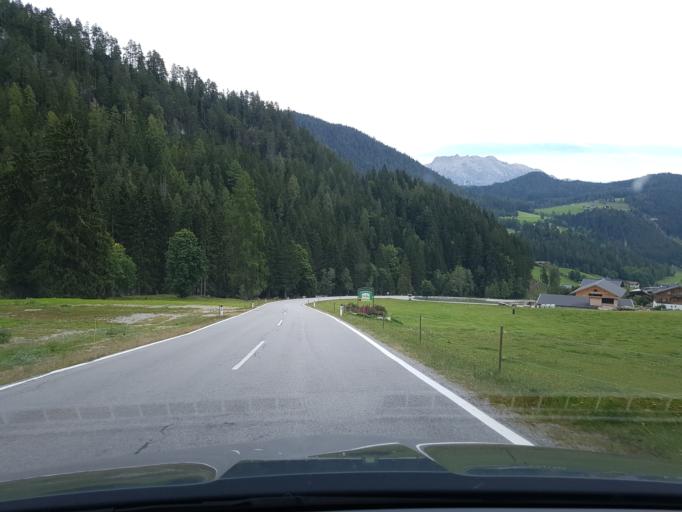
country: AT
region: Salzburg
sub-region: Politischer Bezirk Sankt Johann im Pongau
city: Forstau
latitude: 47.3760
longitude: 13.5414
